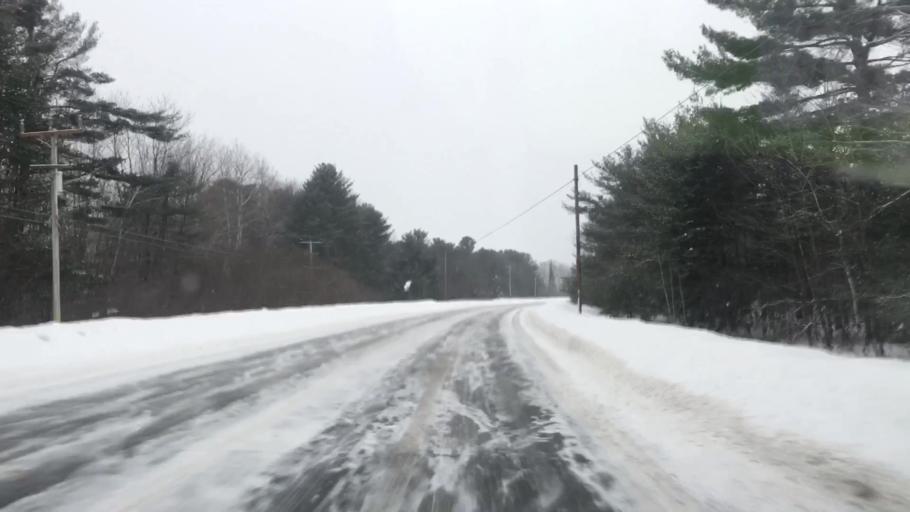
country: US
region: Maine
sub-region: Penobscot County
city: Medway
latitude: 45.5643
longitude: -68.3983
